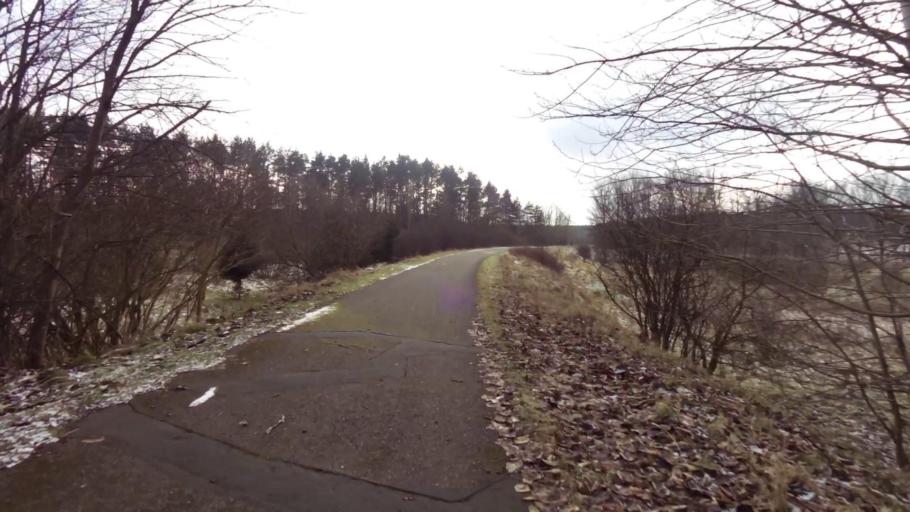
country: PL
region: West Pomeranian Voivodeship
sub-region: Powiat drawski
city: Zlocieniec
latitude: 53.5858
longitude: 16.0471
